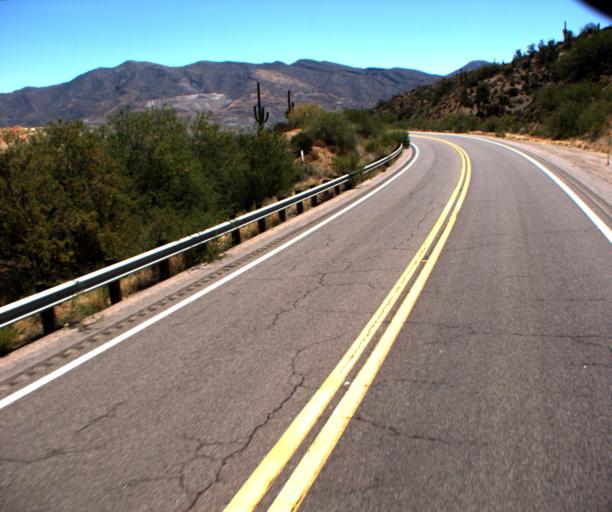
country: US
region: Arizona
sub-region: Pinal County
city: Superior
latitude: 33.1749
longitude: -111.0263
